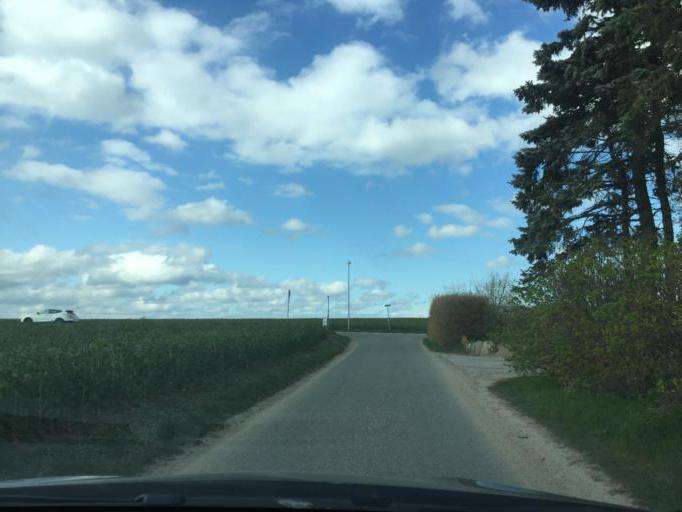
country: DK
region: South Denmark
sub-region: Odense Kommune
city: Hojby
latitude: 55.3325
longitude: 10.4582
